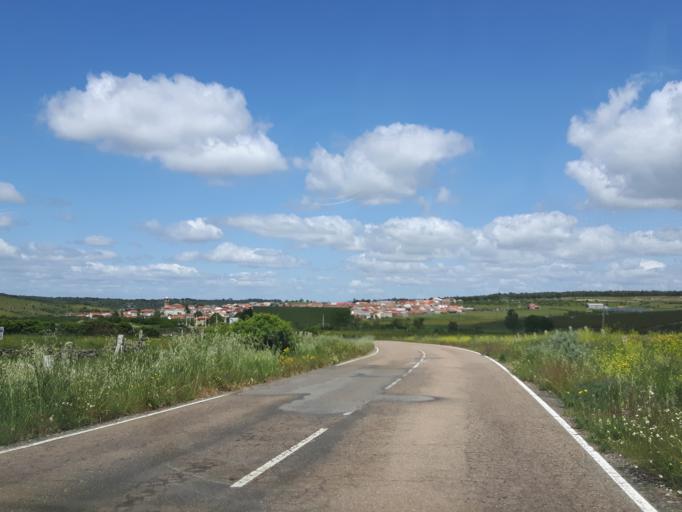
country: ES
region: Castille and Leon
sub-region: Provincia de Salamanca
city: Villar de Ciervo
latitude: 40.7337
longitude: -6.7279
